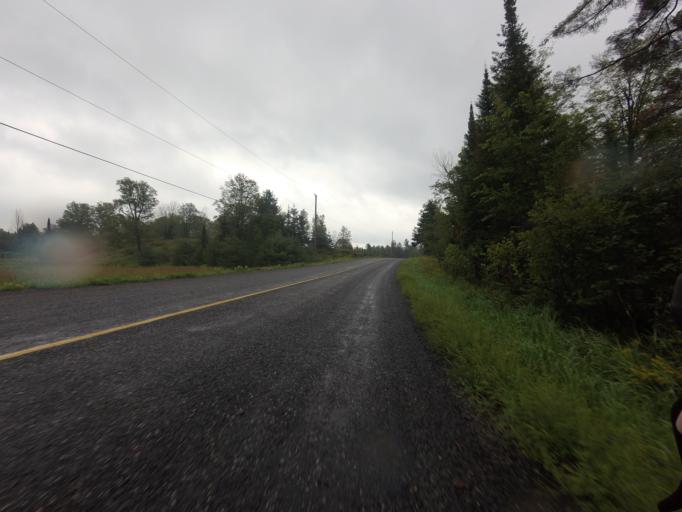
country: CA
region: Ontario
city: Perth
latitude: 45.0639
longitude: -76.5421
